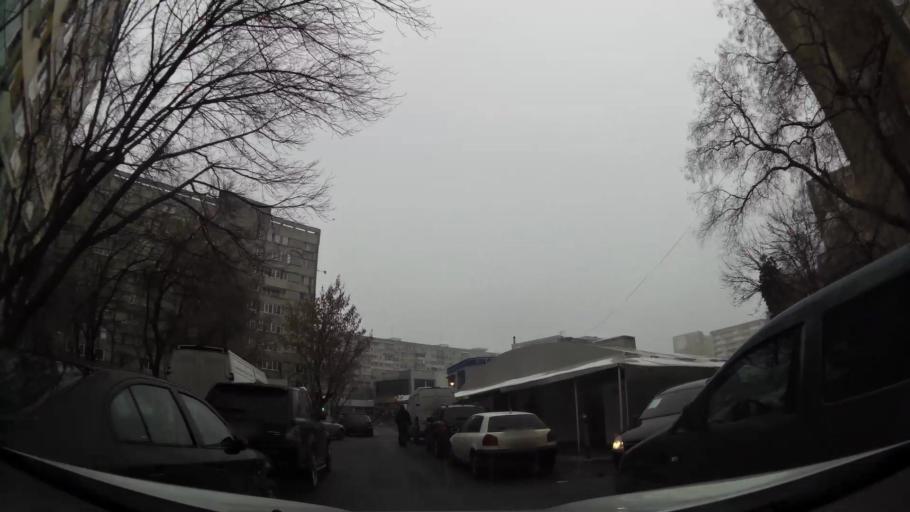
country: RO
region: Ilfov
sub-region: Comuna Chiajna
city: Rosu
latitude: 44.4354
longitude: 26.0304
